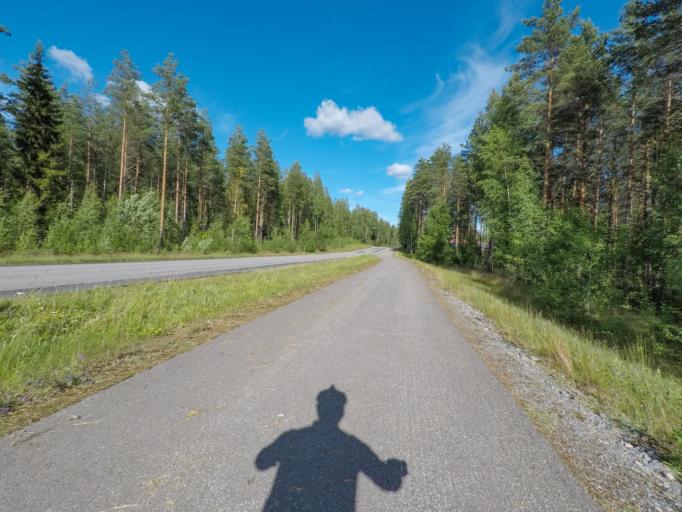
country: FI
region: South Karelia
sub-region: Lappeenranta
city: Joutseno
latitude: 61.1538
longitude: 28.5790
